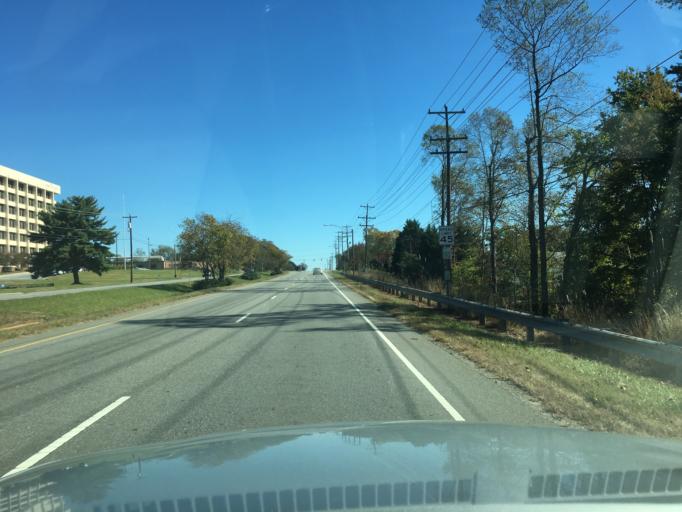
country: US
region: North Carolina
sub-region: Catawba County
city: Hickory
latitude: 35.7284
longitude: -81.3053
